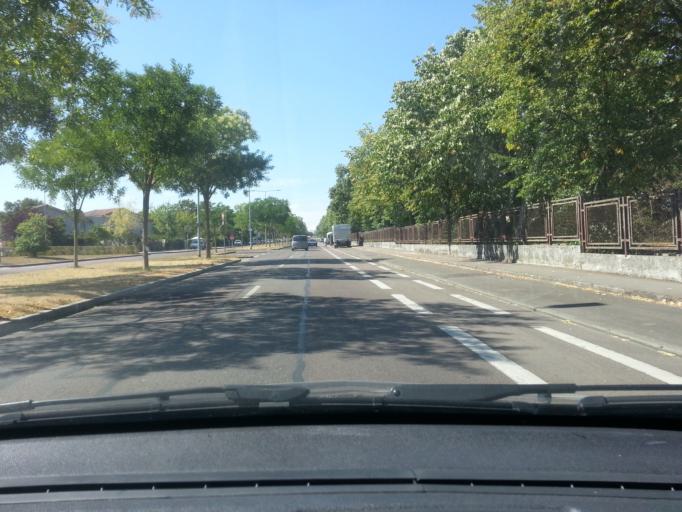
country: FR
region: Bourgogne
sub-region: Departement de la Cote-d'Or
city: Fontaine-les-Dijon
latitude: 47.3436
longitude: 5.0492
